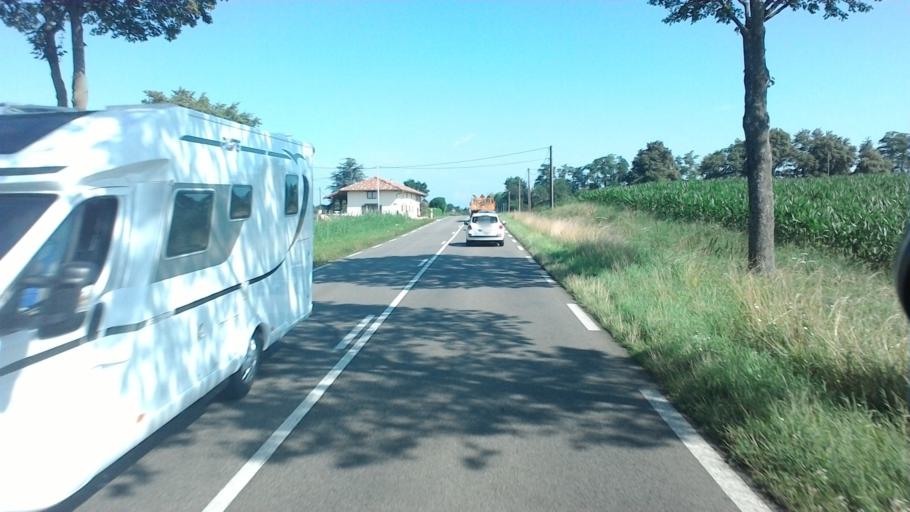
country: FR
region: Rhone-Alpes
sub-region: Departement de l'Ain
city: Saint-Trivier-de-Courtes
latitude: 46.4407
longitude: 5.0913
